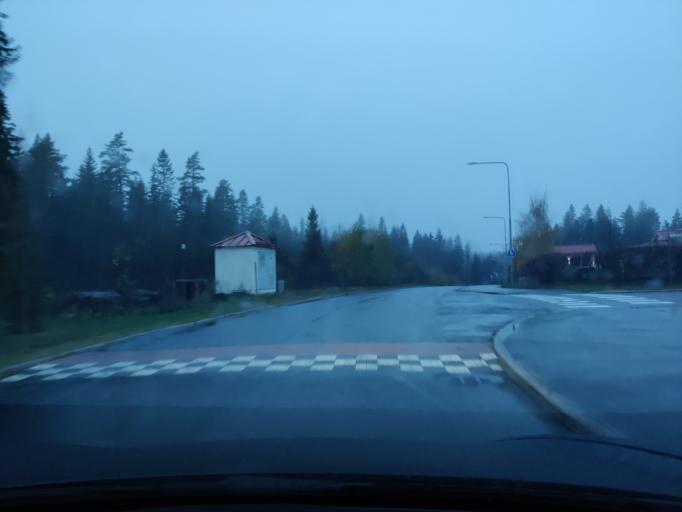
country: FI
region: Northern Savo
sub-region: Kuopio
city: Kuopio
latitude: 62.8287
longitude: 27.7178
